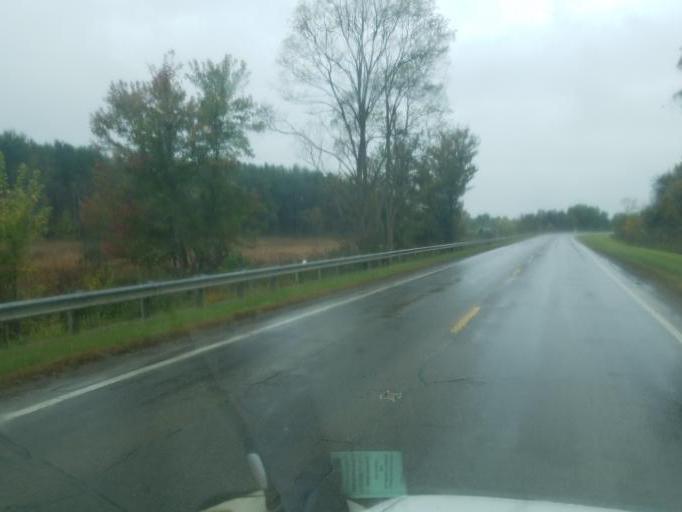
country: US
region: Ohio
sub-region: Holmes County
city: Millersburg
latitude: 40.6238
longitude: -81.9227
